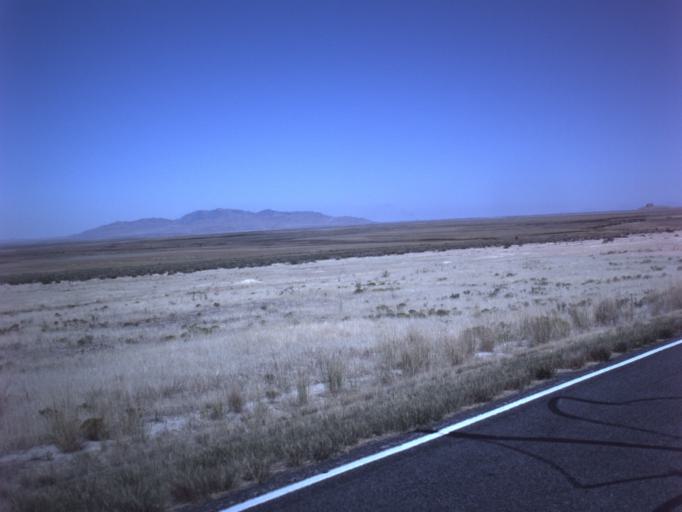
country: US
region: Utah
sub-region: Tooele County
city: Grantsville
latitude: 40.6033
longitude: -112.7114
